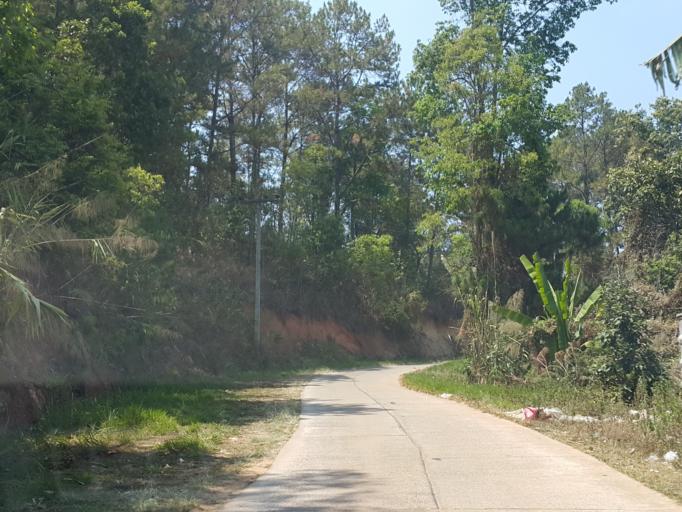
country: TH
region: Chiang Mai
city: Samoeng
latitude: 18.8821
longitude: 98.7840
